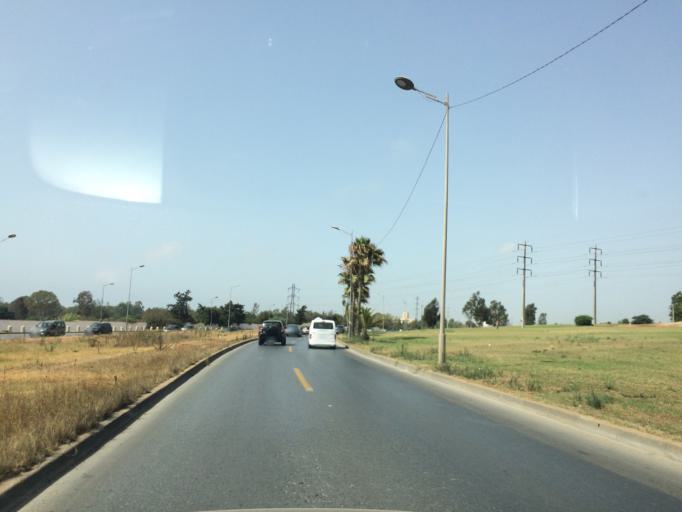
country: MA
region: Rabat-Sale-Zemmour-Zaer
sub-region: Rabat
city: Rabat
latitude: 33.9722
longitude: -6.8647
